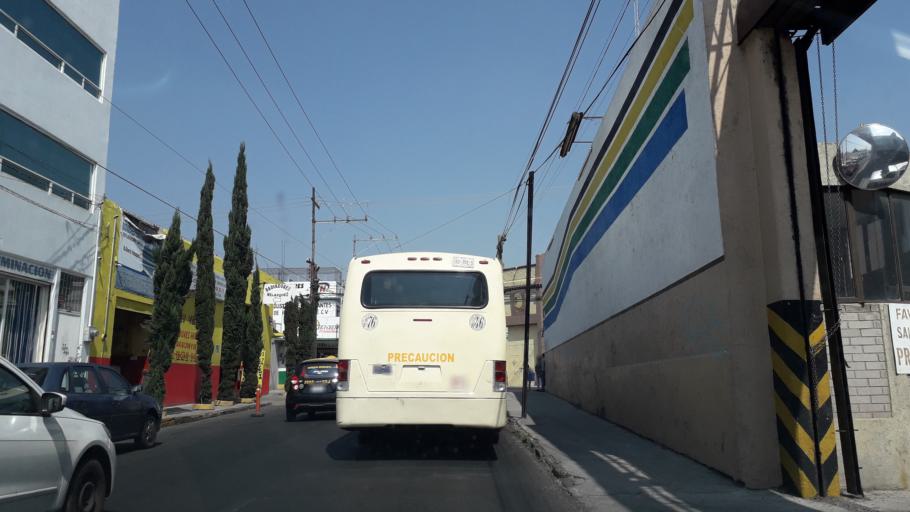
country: MX
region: Puebla
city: Puebla
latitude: 19.0527
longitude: -98.2125
